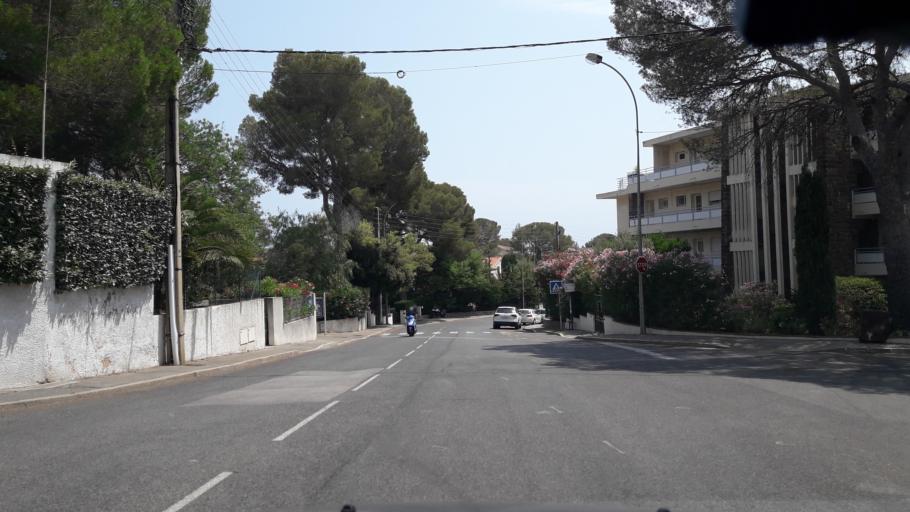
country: FR
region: Provence-Alpes-Cote d'Azur
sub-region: Departement du Var
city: Saint-Raphael
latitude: 43.4191
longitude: 6.8069
